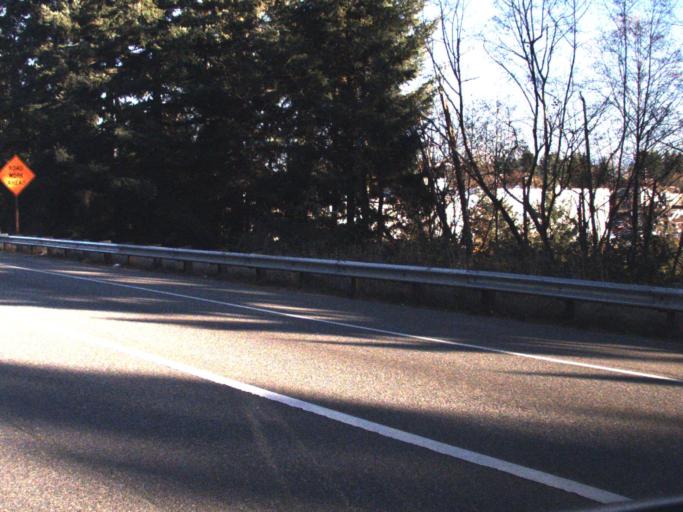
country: US
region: Washington
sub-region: Snohomish County
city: Mill Creek
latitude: 47.9074
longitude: -122.2108
